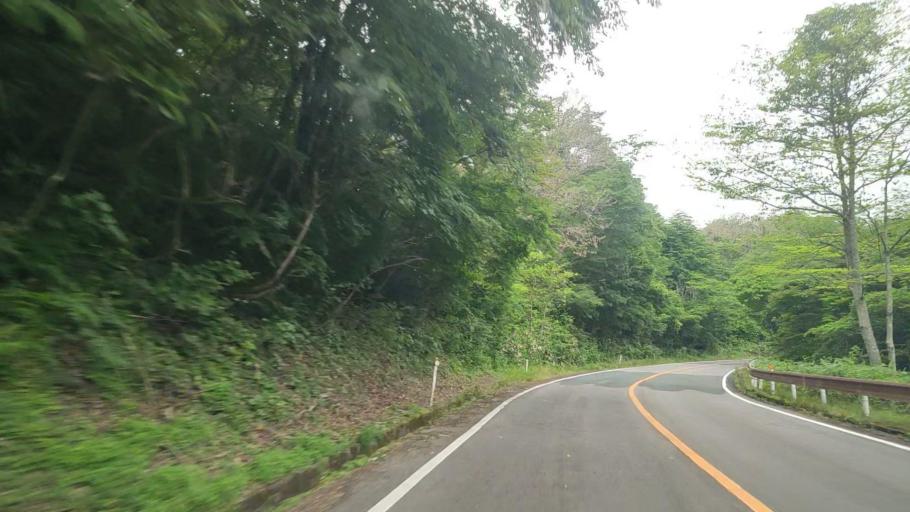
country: JP
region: Tottori
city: Kurayoshi
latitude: 35.3044
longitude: 133.6195
